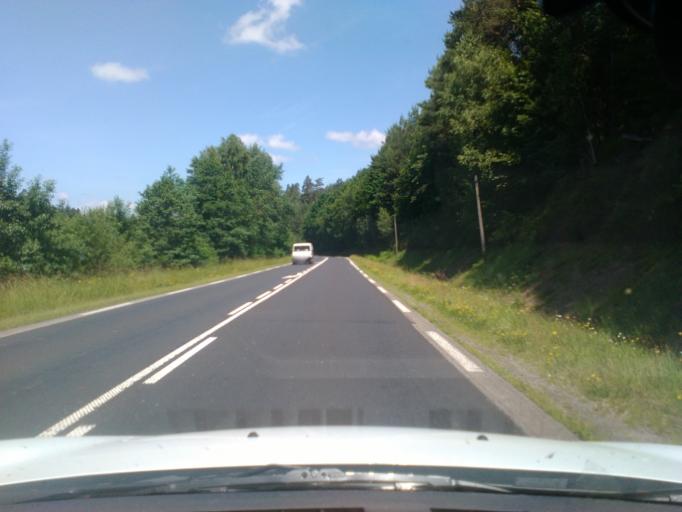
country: FR
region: Lorraine
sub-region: Departement des Vosges
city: Bruyeres
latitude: 48.2312
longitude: 6.7043
